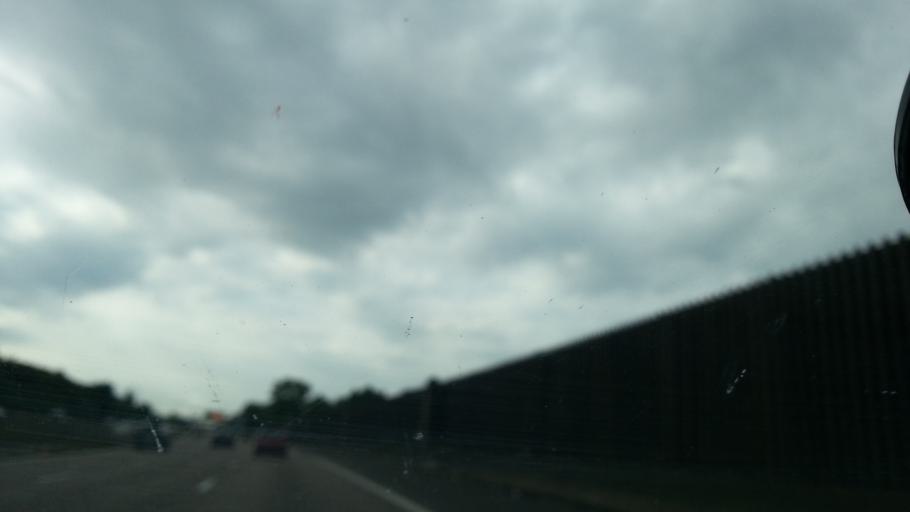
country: FR
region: Bourgogne
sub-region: Departement de Saone-et-Loire
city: Saint-Remy
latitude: 46.7722
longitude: 4.8198
